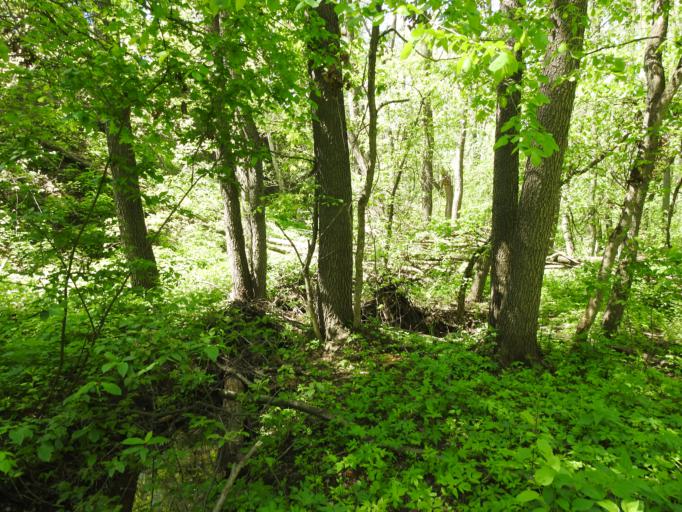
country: RU
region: Saratov
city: Krasnyy Oktyabr'
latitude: 51.5930
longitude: 45.7252
